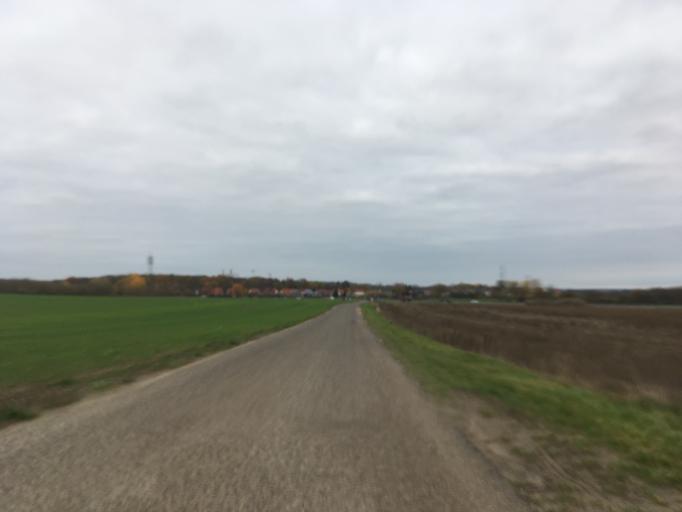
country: DE
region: Brandenburg
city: Frankfurt (Oder)
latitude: 52.3041
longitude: 14.5265
